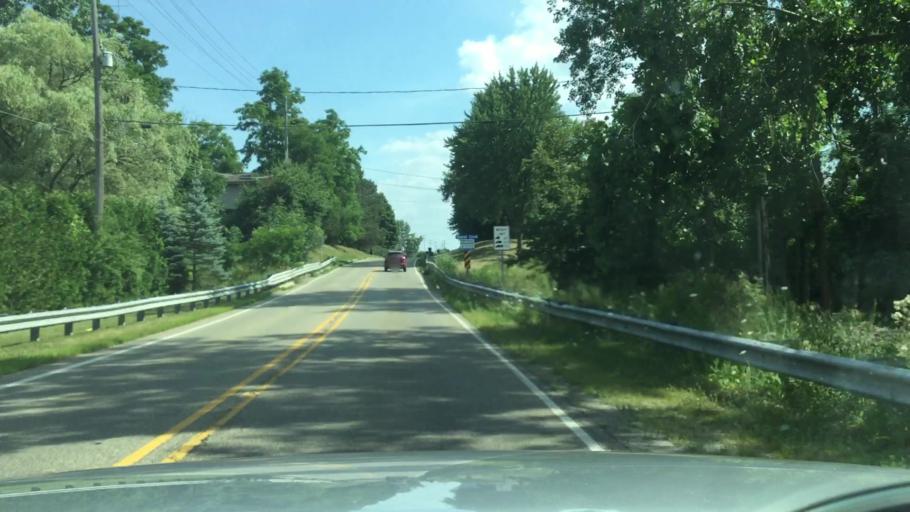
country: US
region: Michigan
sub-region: Genesee County
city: Grand Blanc
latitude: 42.9363
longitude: -83.5975
